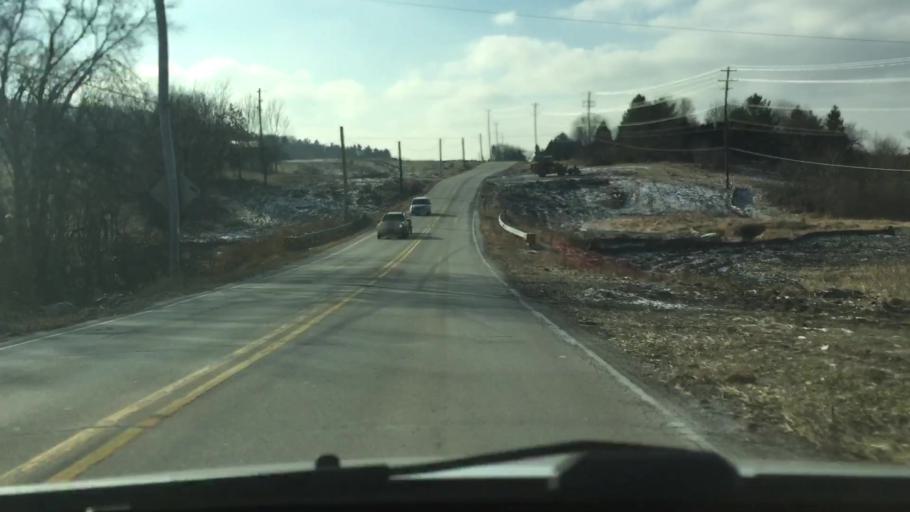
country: US
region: Wisconsin
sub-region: Waukesha County
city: Waukesha
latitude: 43.0110
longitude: -88.2865
